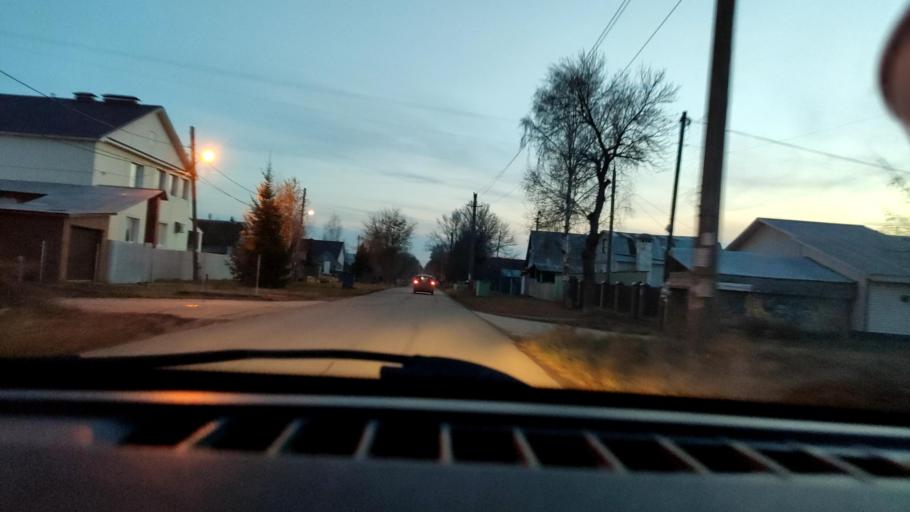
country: RU
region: Samara
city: Petra-Dubrava
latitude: 53.2617
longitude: 50.3300
